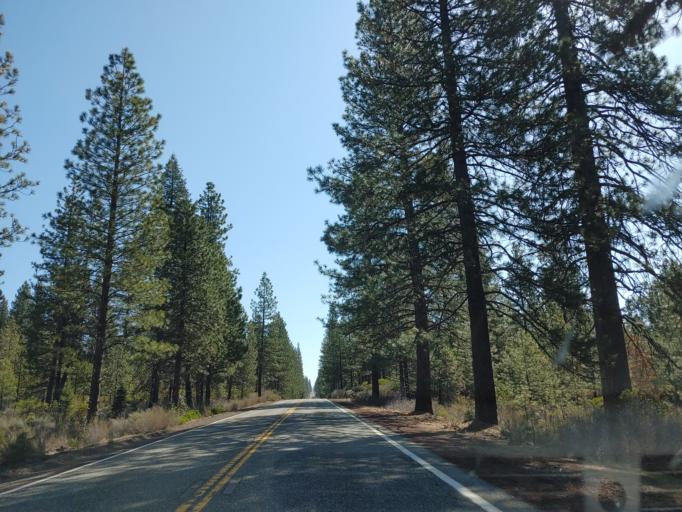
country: US
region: California
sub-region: Siskiyou County
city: McCloud
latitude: 41.2551
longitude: -122.0589
